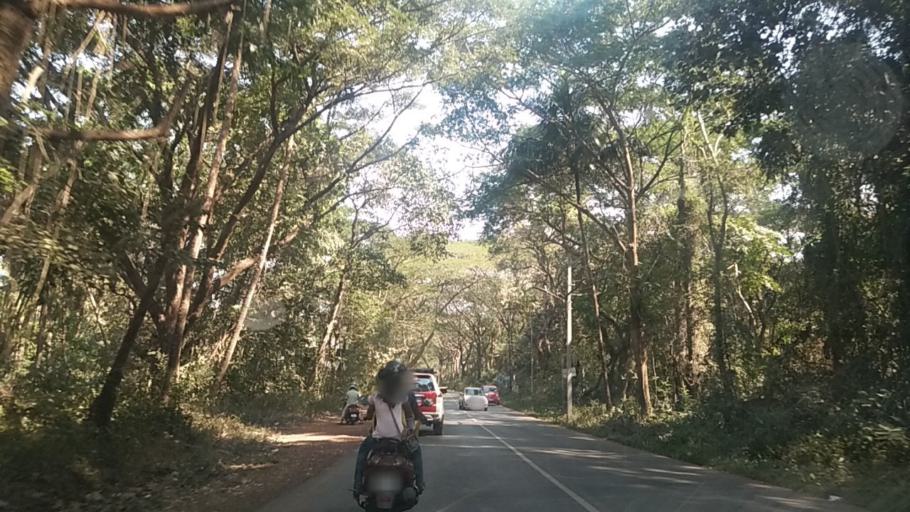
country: IN
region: Goa
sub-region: North Goa
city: Goa Velha
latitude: 15.5002
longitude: 73.8980
